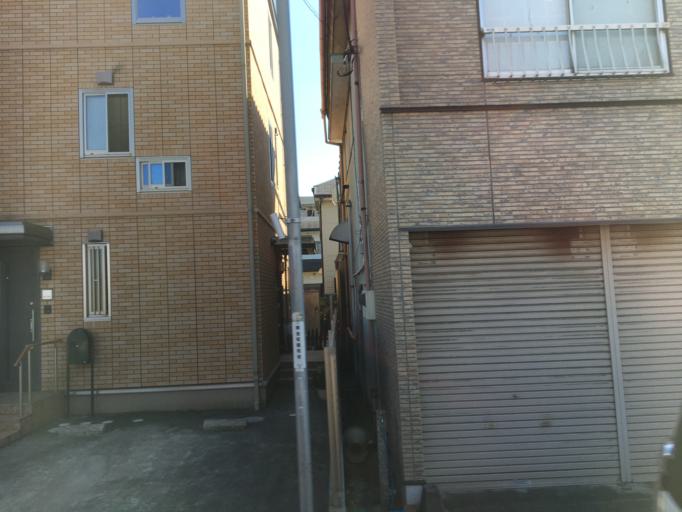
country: JP
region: Saitama
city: Sakado
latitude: 35.9605
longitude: 139.3935
